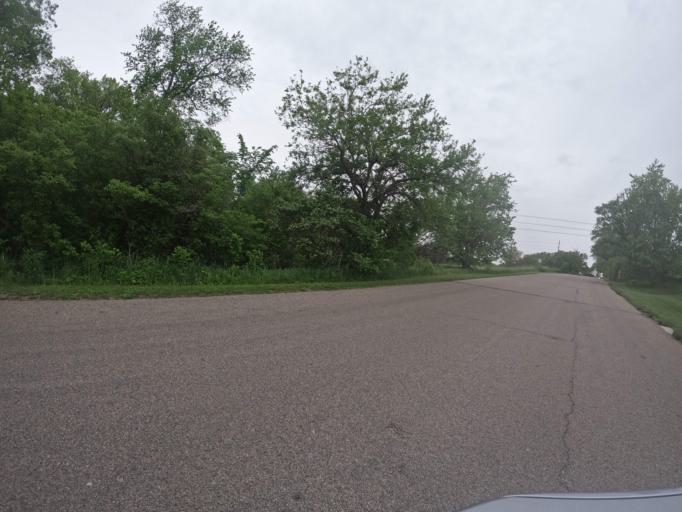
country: US
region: Nebraska
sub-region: Sarpy County
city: Offutt Air Force Base
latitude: 41.0508
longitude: -95.9627
